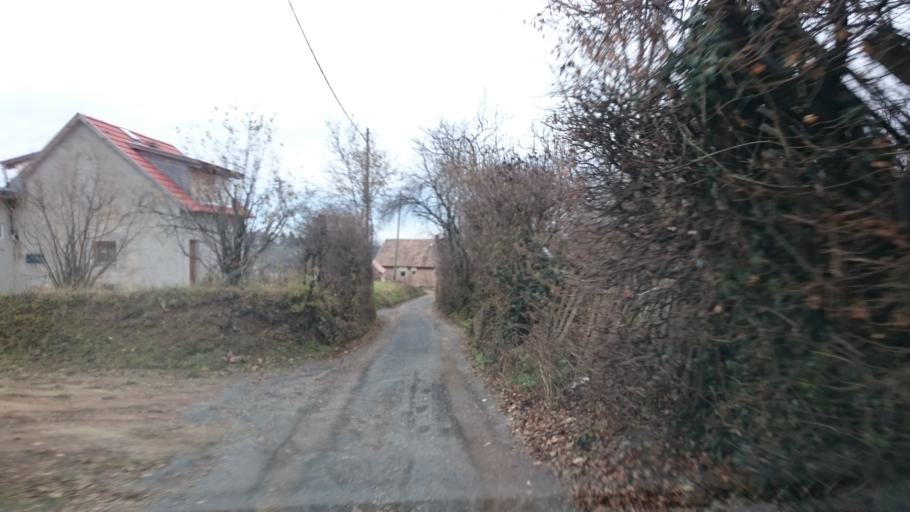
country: HU
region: Baranya
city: Pellerd
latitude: 46.0774
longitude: 18.1748
